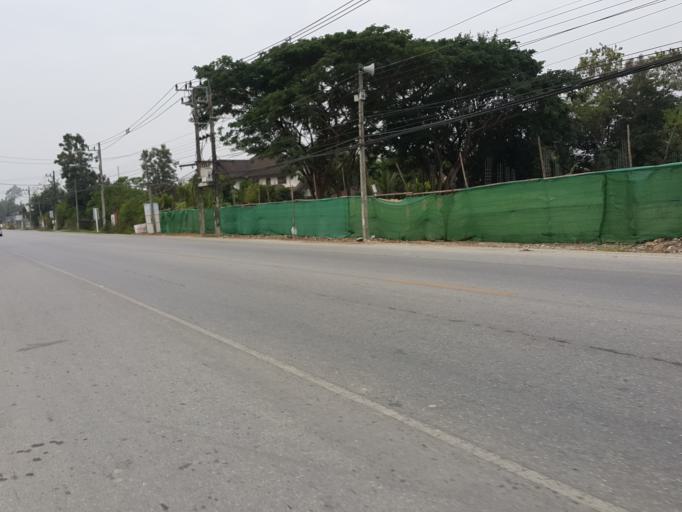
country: TH
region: Chiang Mai
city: San Kamphaeng
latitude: 18.7868
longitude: 99.0974
